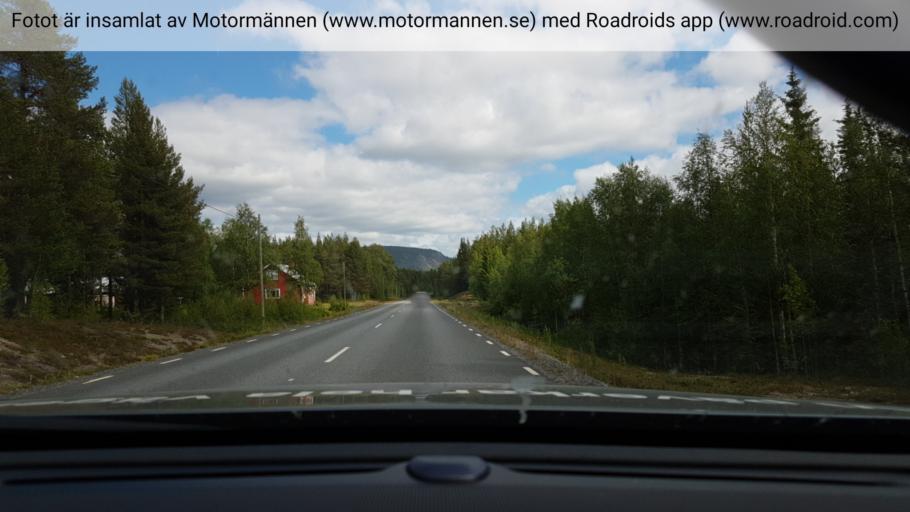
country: SE
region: Vaesterbotten
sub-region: Sorsele Kommun
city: Sorsele
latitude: 65.6868
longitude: 17.3244
